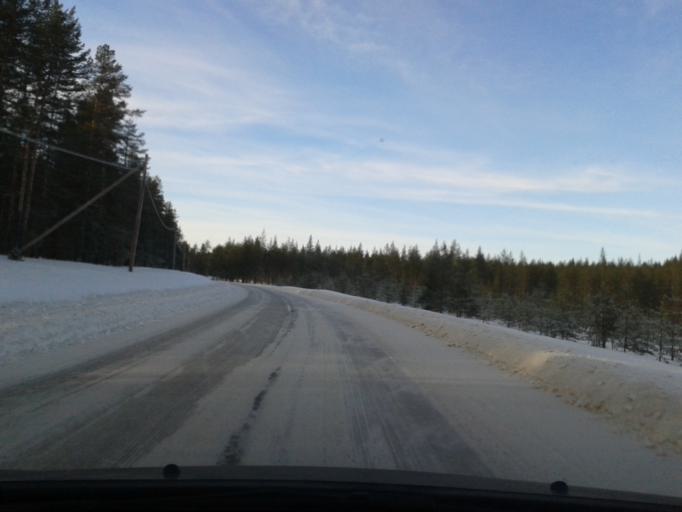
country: SE
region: Vaesternorrland
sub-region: OErnskoeldsviks Kommun
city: Bredbyn
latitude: 63.6554
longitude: 17.8753
